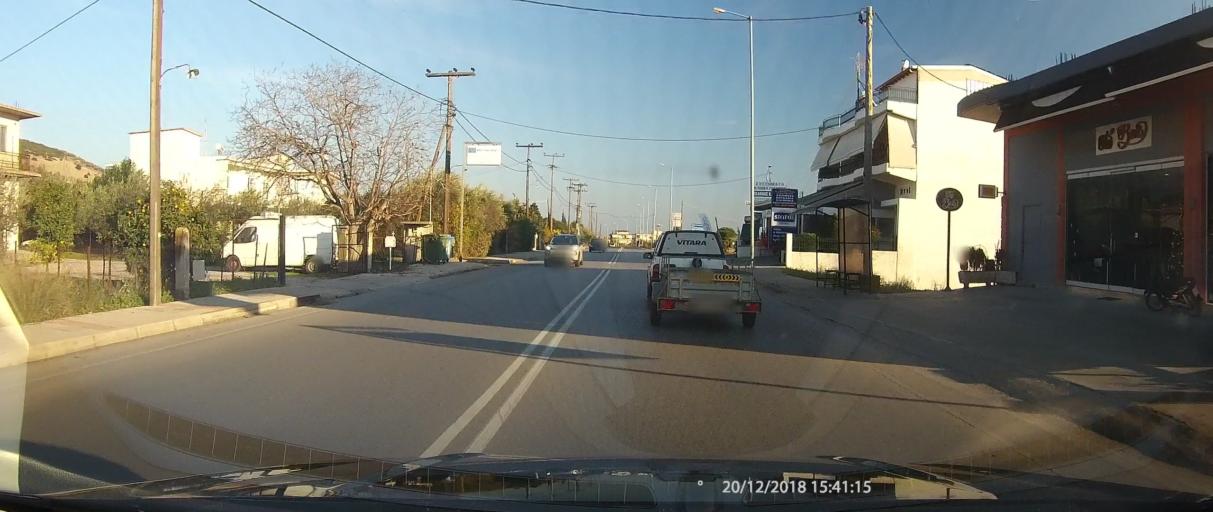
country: GR
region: Central Greece
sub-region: Nomos Fthiotidos
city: Stavros
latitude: 38.8906
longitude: 22.3821
